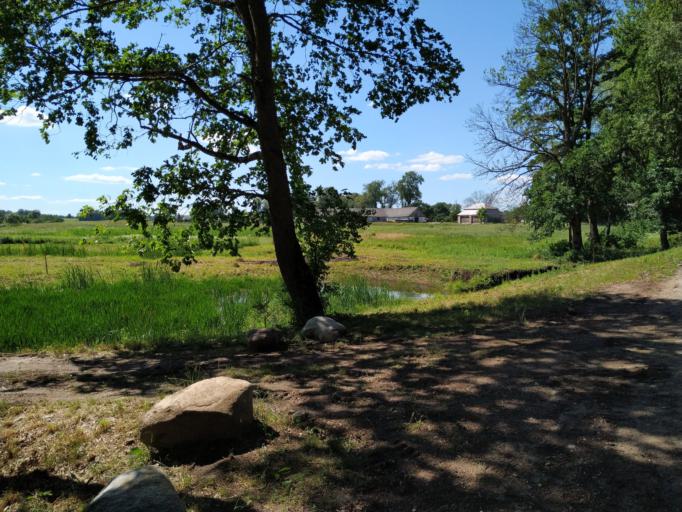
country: LT
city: Nemencine
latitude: 54.8512
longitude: 25.3394
